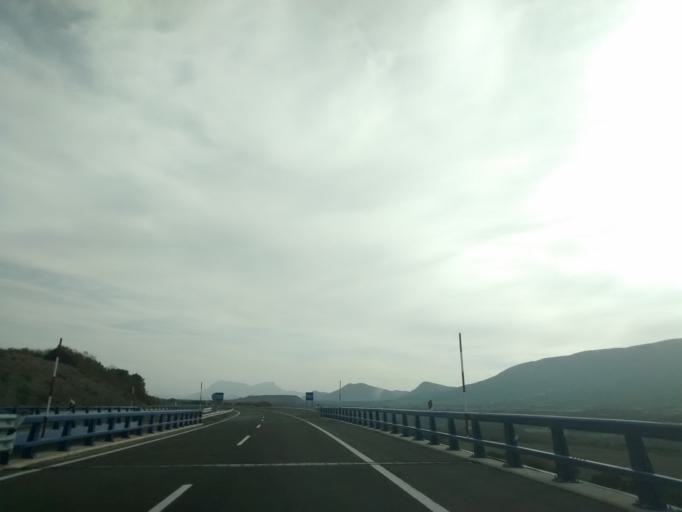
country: ES
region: Aragon
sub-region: Provincia de Zaragoza
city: Artieda
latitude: 42.6101
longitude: -0.9844
